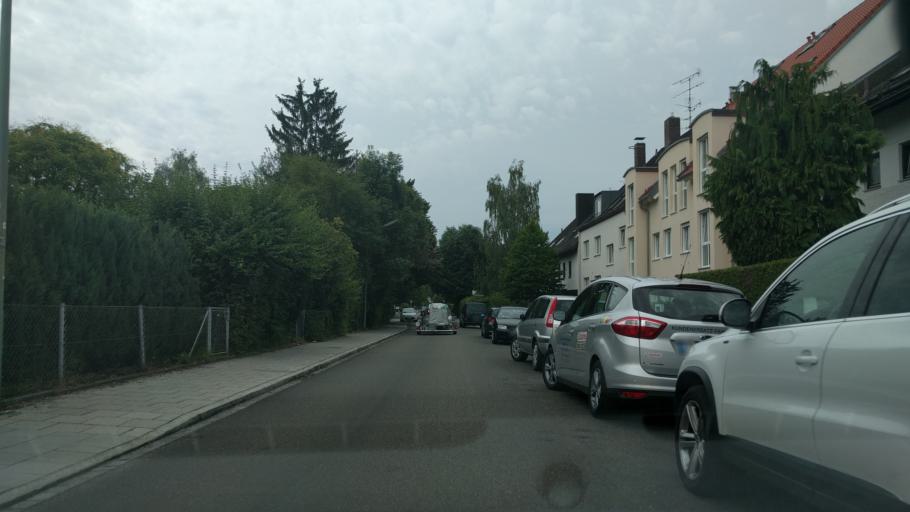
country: DE
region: Bavaria
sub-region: Upper Bavaria
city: Munich
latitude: 48.1041
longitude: 11.5712
